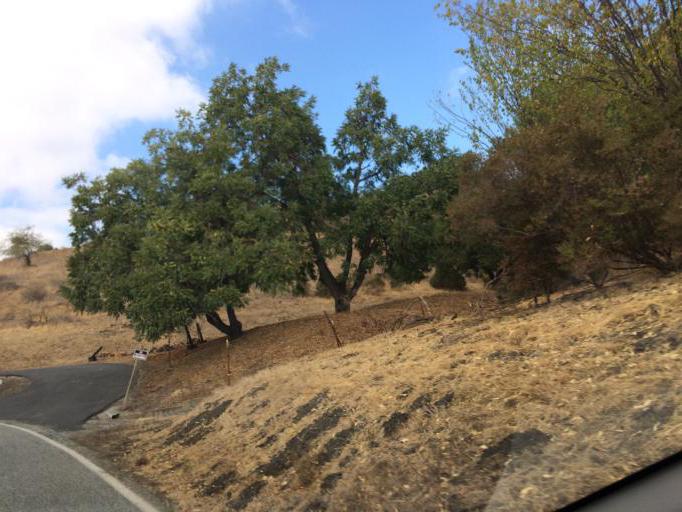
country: US
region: California
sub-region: Santa Clara County
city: East Foothills
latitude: 37.3815
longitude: -121.7983
